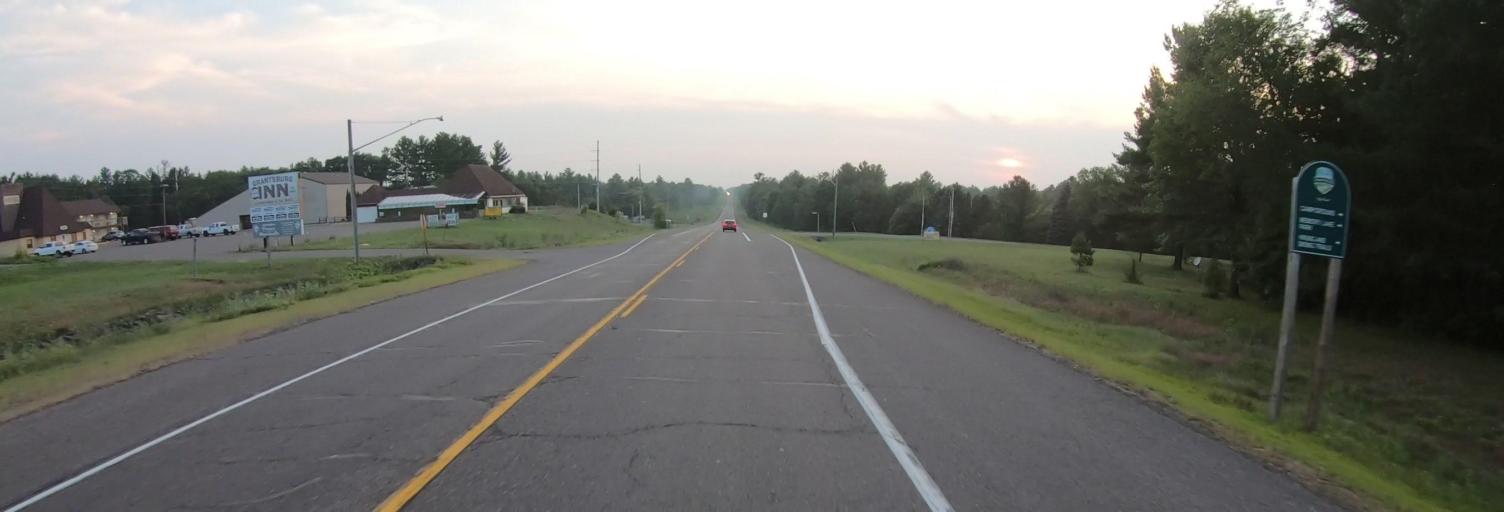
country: US
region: Wisconsin
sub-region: Burnett County
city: Grantsburg
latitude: 45.7730
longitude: -92.6983
